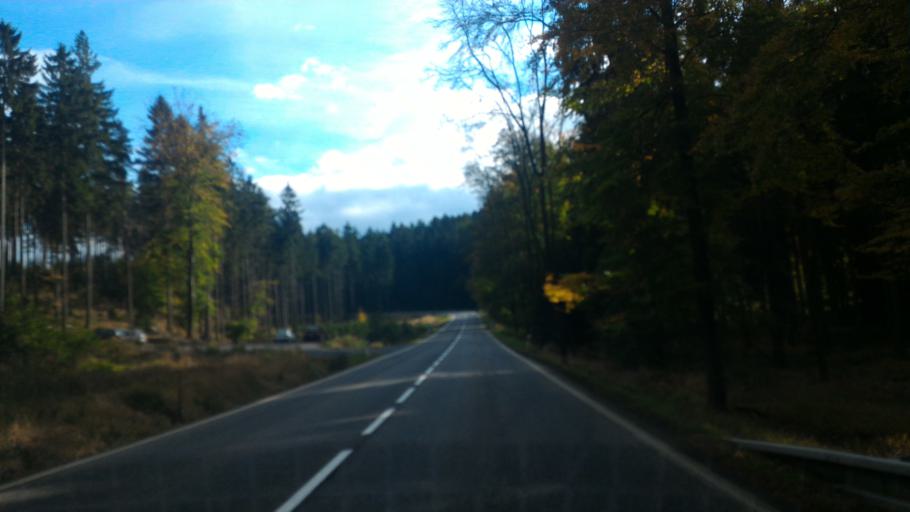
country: CZ
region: Ustecky
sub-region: Okres Decin
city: Chribska
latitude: 50.8391
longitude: 14.4837
